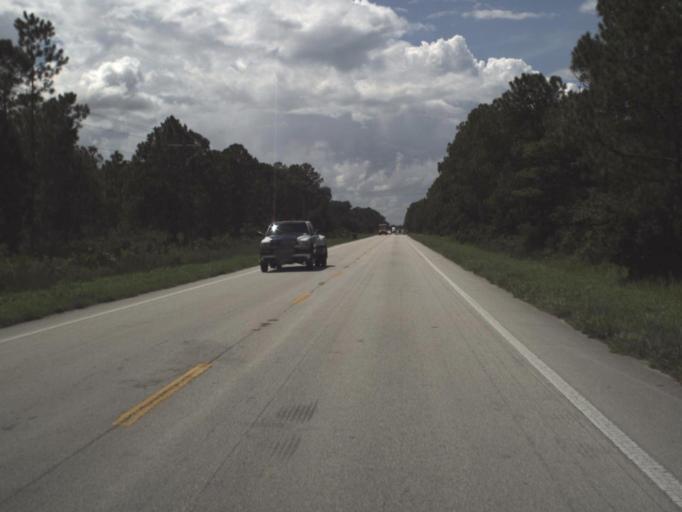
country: US
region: Florida
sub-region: Polk County
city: Babson Park
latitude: 27.8058
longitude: -81.2944
